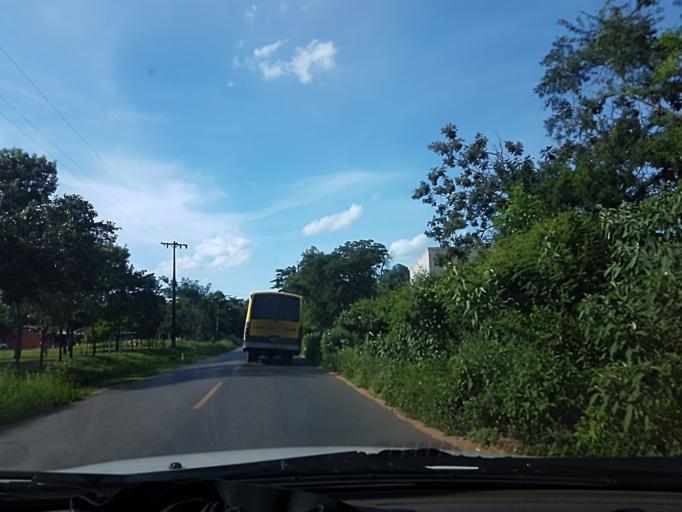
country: PY
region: Central
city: Limpio
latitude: -25.2125
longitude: -57.4487
